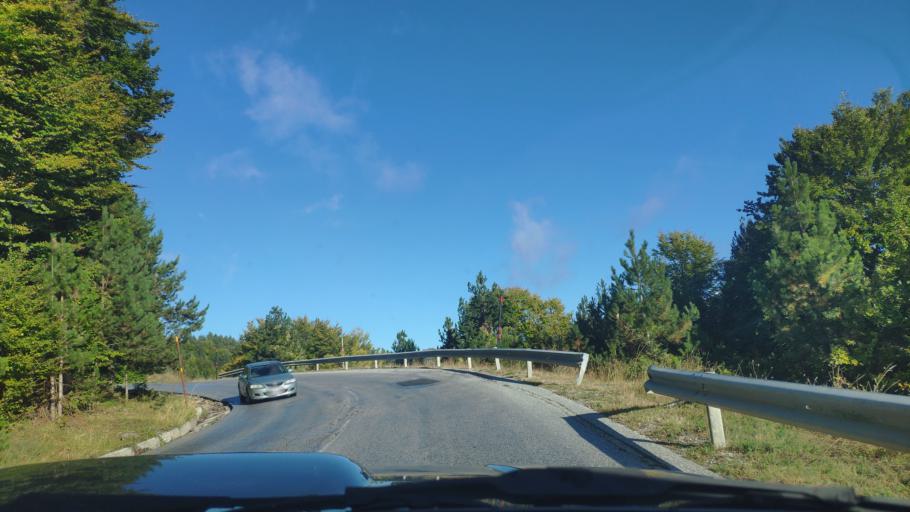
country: GR
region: Epirus
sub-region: Nomos Ioanninon
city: Metsovo
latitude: 39.7768
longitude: 21.1751
